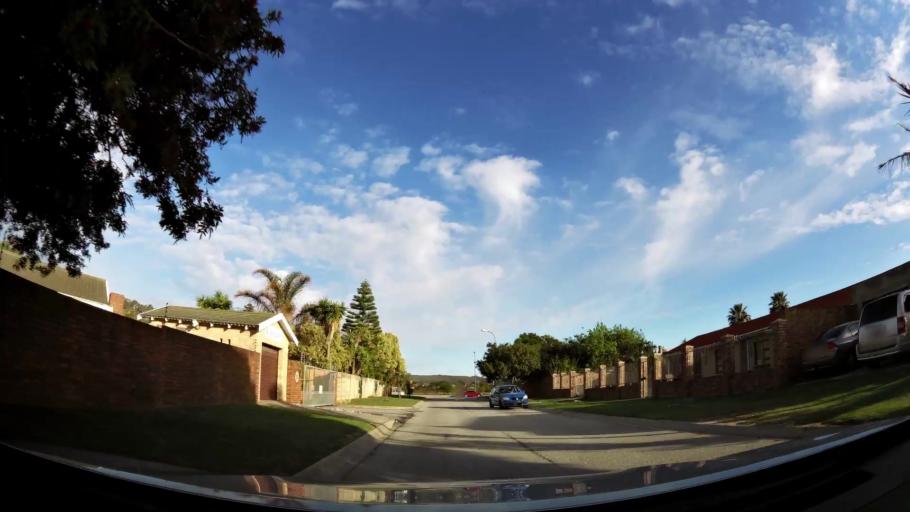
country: ZA
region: Eastern Cape
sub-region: Nelson Mandela Bay Metropolitan Municipality
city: Port Elizabeth
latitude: -33.9576
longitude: 25.4952
